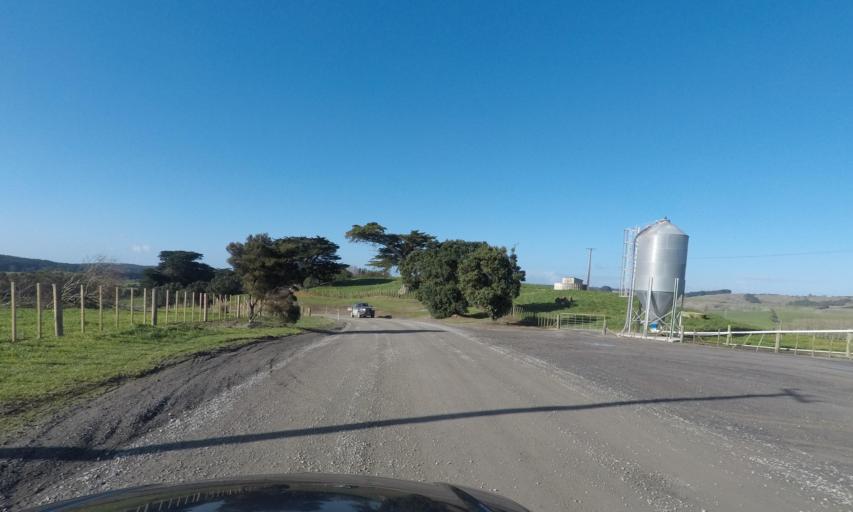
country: NZ
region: Auckland
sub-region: Auckland
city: Wellsford
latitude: -36.1442
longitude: 174.5969
